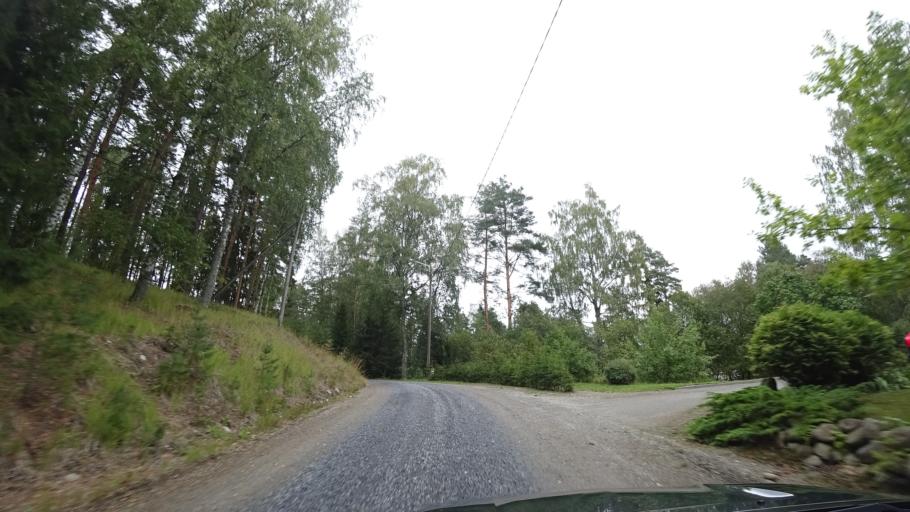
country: FI
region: Haeme
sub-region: Haemeenlinna
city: Lammi
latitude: 61.1225
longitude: 24.9832
